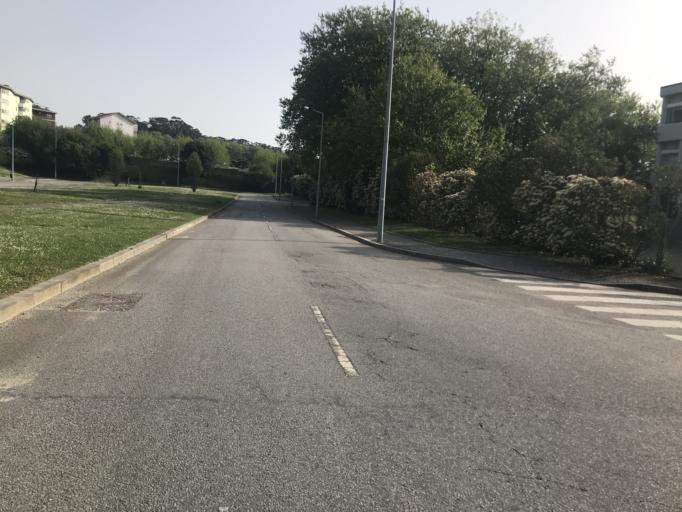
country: PT
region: Porto
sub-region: Matosinhos
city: Matosinhos
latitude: 41.1759
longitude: -8.6763
